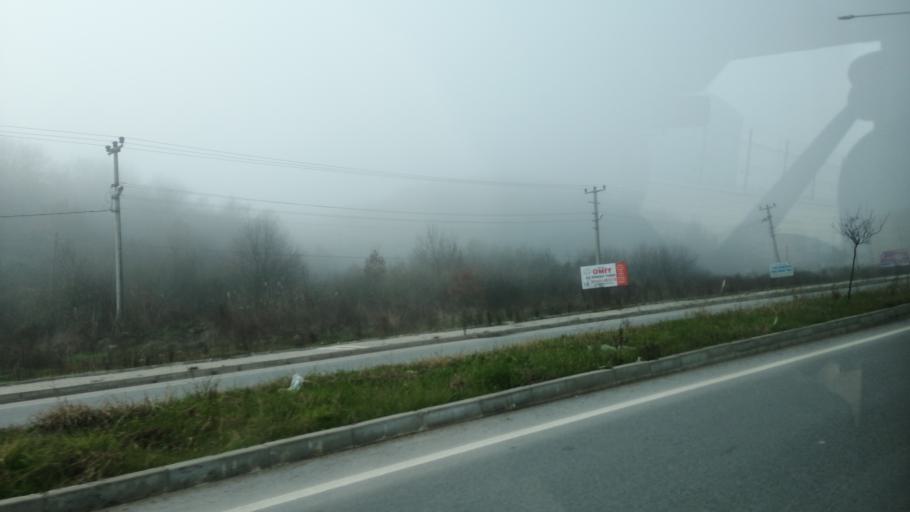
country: TR
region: Yalova
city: Kadikoy
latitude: 40.6499
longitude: 29.2267
